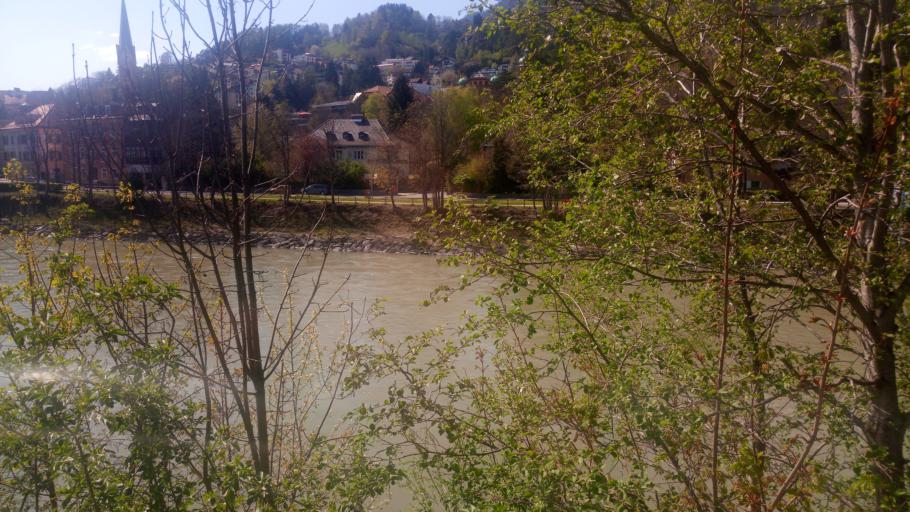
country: AT
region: Tyrol
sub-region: Innsbruck Stadt
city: Innsbruck
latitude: 47.2754
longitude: 11.3972
